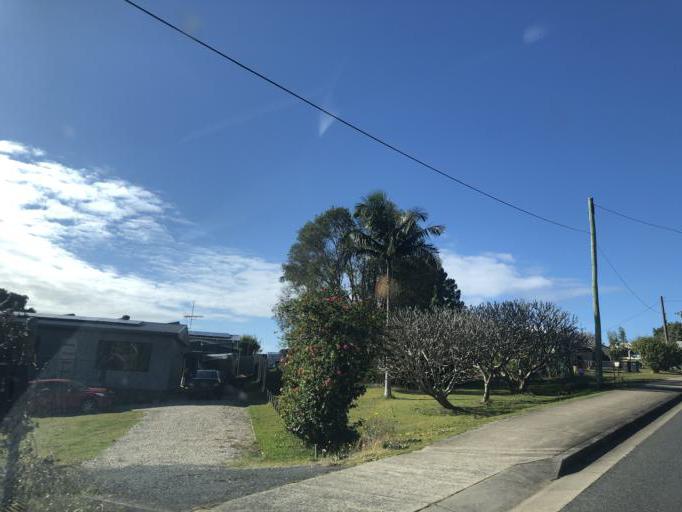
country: AU
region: New South Wales
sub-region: Coffs Harbour
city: Toormina
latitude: -30.3399
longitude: 153.0838
